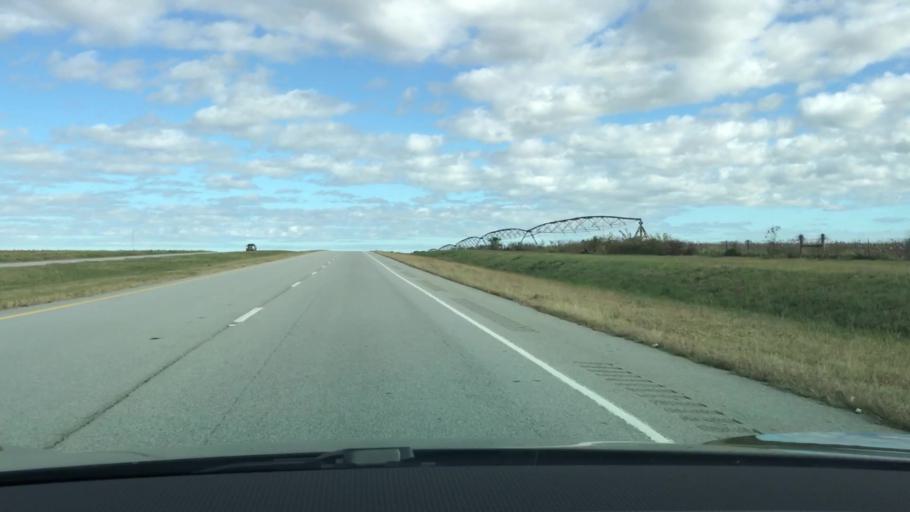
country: US
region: Georgia
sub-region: Jefferson County
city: Wadley
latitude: 32.8231
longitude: -82.4041
